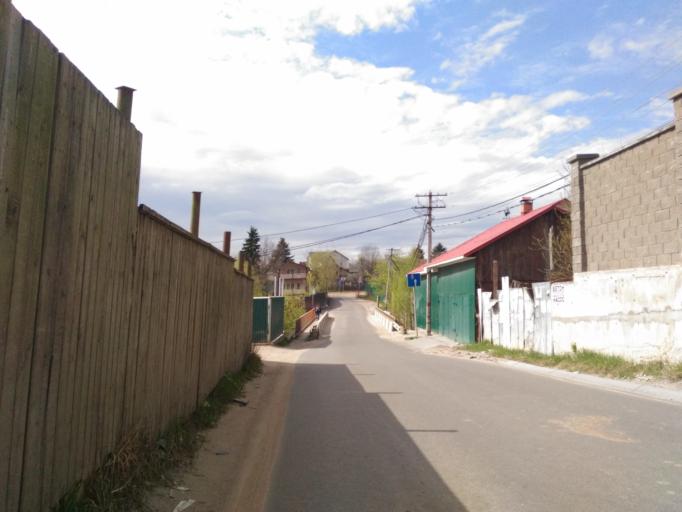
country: RU
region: Moskovskaya
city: Nakhabino
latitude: 55.8485
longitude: 37.1533
